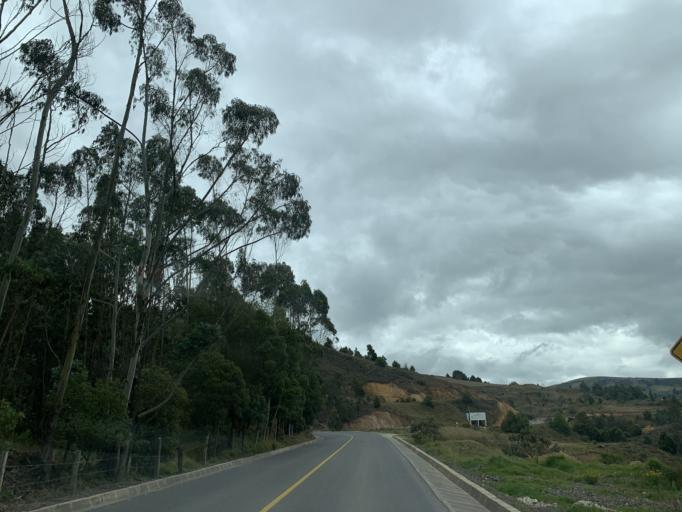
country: CO
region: Boyaca
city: Tunja
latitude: 5.5304
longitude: -73.3266
